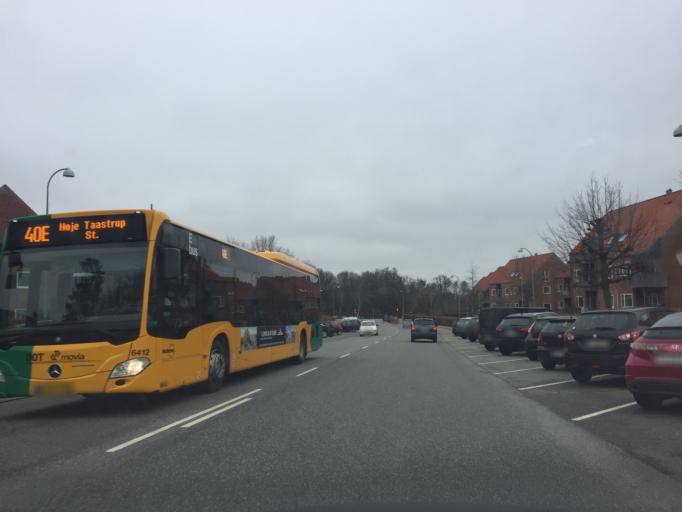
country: DK
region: Capital Region
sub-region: Gladsaxe Municipality
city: Buddinge
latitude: 55.7631
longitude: 12.4545
